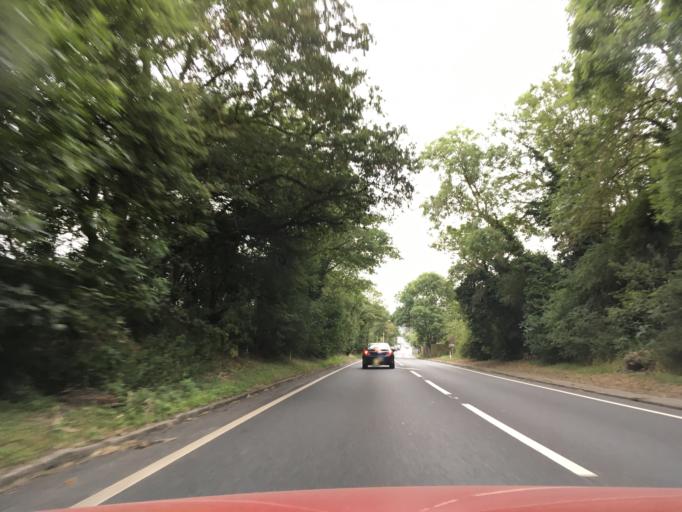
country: GB
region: England
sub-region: Central Bedfordshire
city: Hockliffe
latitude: 51.9367
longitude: -0.5950
